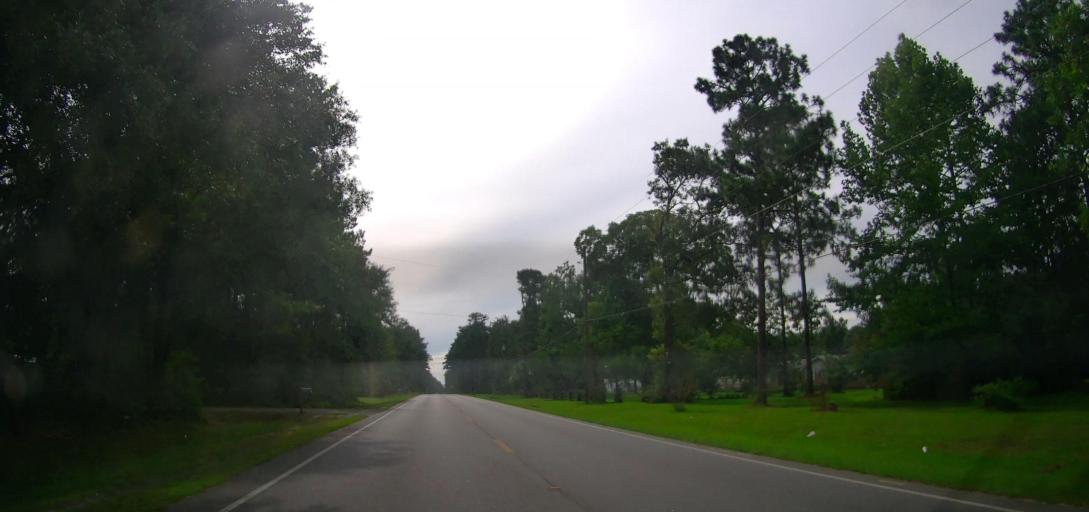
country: US
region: Georgia
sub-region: Wayne County
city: Jesup
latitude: 31.6620
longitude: -81.8521
